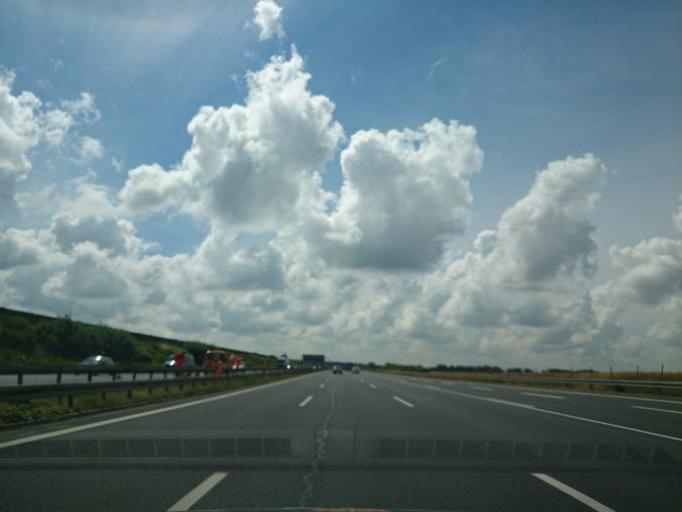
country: DE
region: Brandenburg
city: Schulzendorf
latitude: 52.3579
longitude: 13.5491
